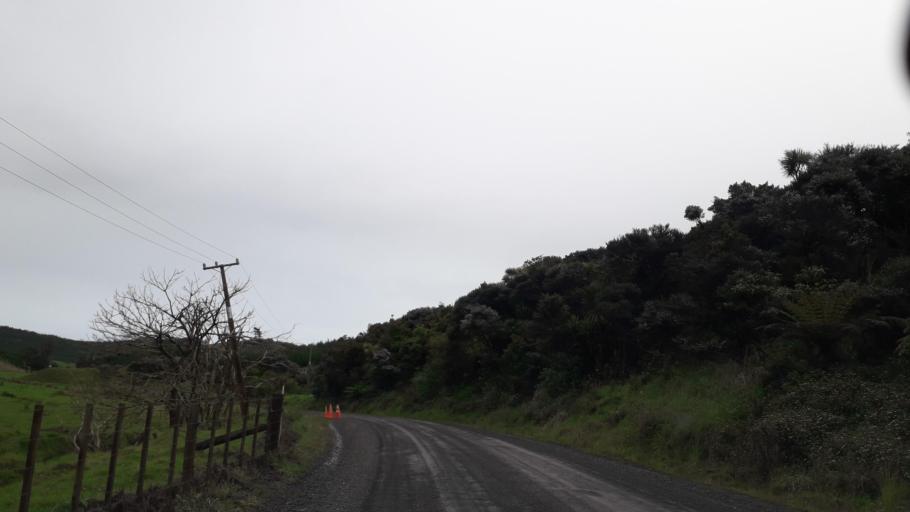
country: NZ
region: Northland
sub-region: Far North District
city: Ahipara
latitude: -35.4277
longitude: 173.3538
